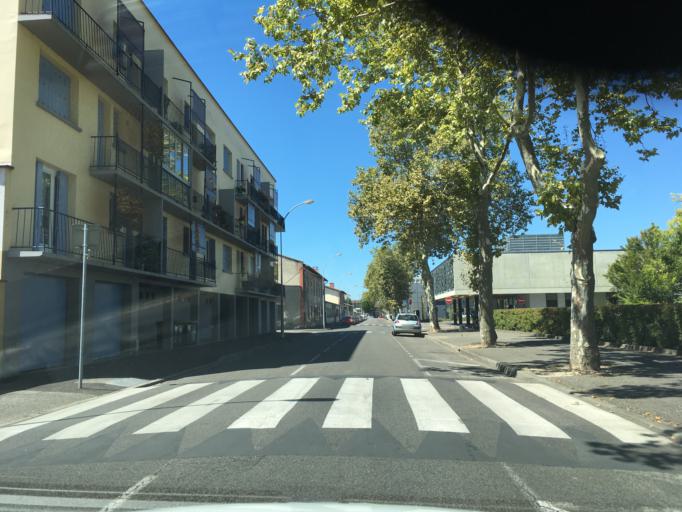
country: FR
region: Midi-Pyrenees
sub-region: Departement du Tarn-et-Garonne
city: Montauban
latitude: 44.0242
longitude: 1.3594
